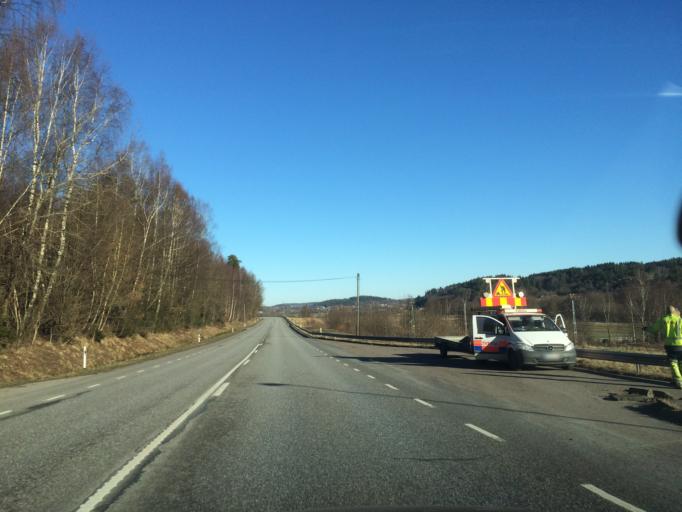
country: SE
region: Vaestra Goetaland
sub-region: Molndal
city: Lindome
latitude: 57.5491
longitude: 12.0949
